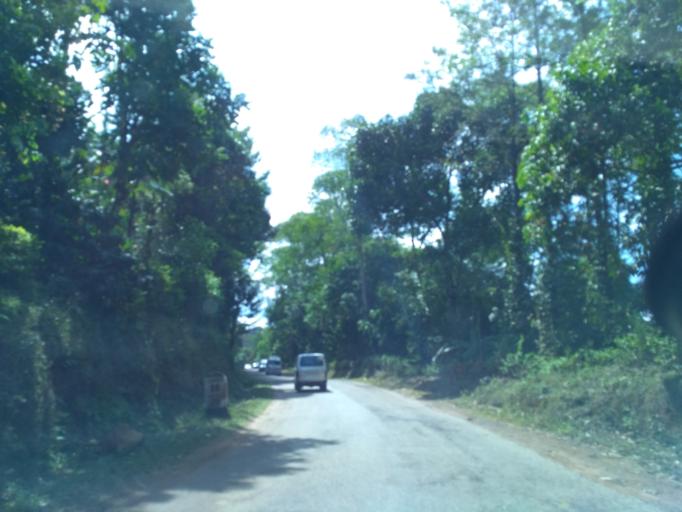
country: IN
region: Karnataka
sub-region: Kodagu
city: Madikeri
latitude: 12.3847
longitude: 75.7099
